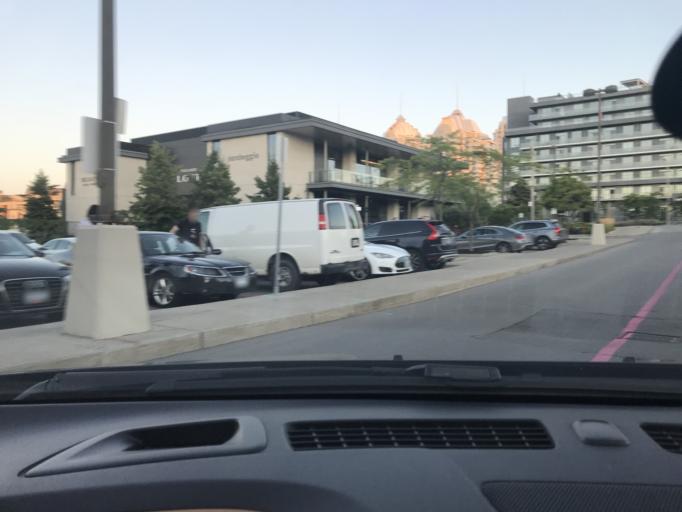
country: CA
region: Ontario
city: Willowdale
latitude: 43.7680
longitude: -79.3862
